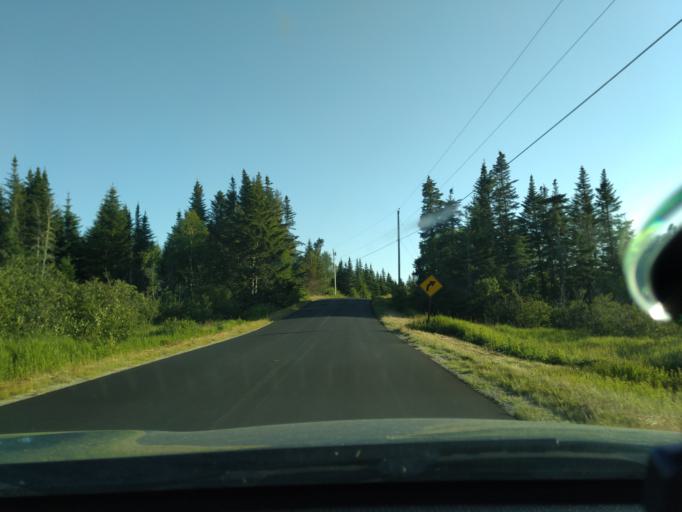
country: US
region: Maine
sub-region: Washington County
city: Machiasport
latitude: 44.6710
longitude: -67.1955
